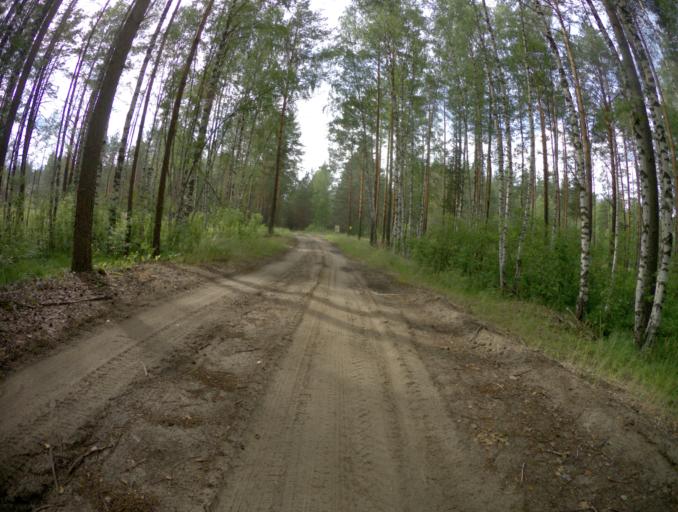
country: RU
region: Nizjnij Novgorod
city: Frolishchi
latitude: 56.3197
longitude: 42.6441
